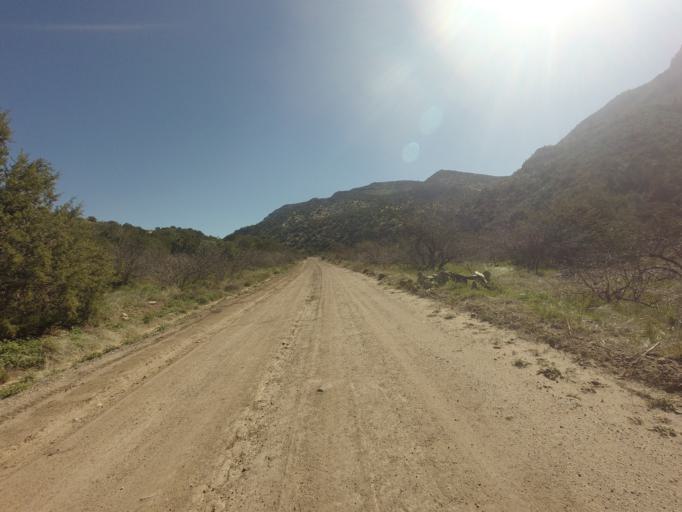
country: US
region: Arizona
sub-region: Gila County
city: Pine
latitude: 34.3937
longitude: -111.6344
